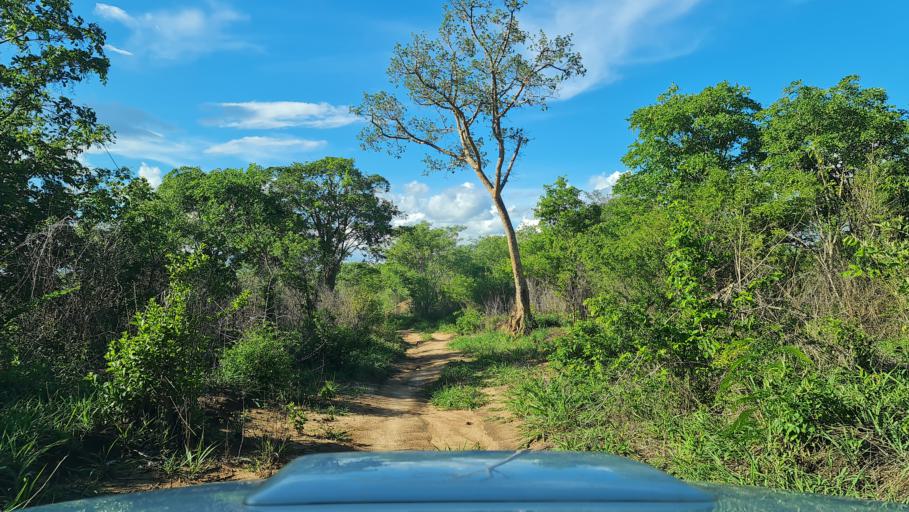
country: MZ
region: Nampula
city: Ilha de Mocambique
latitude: -15.2588
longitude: 40.1843
